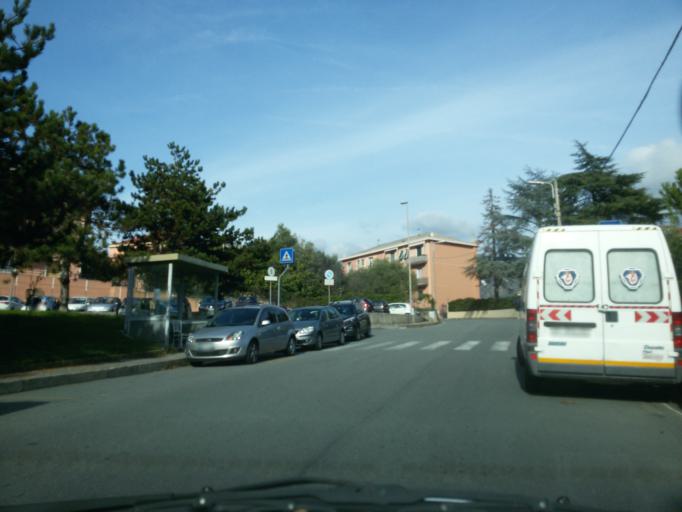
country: IT
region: Liguria
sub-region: Provincia di Genova
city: Piccarello
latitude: 44.4557
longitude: 8.9728
